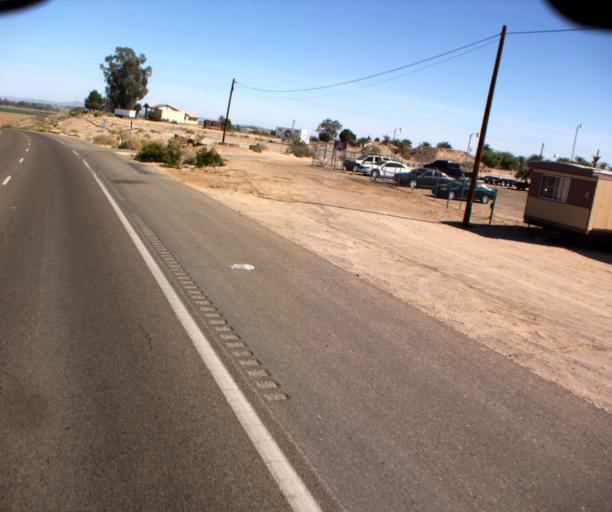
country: US
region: Arizona
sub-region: Yuma County
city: Somerton
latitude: 32.6142
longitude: -114.6496
